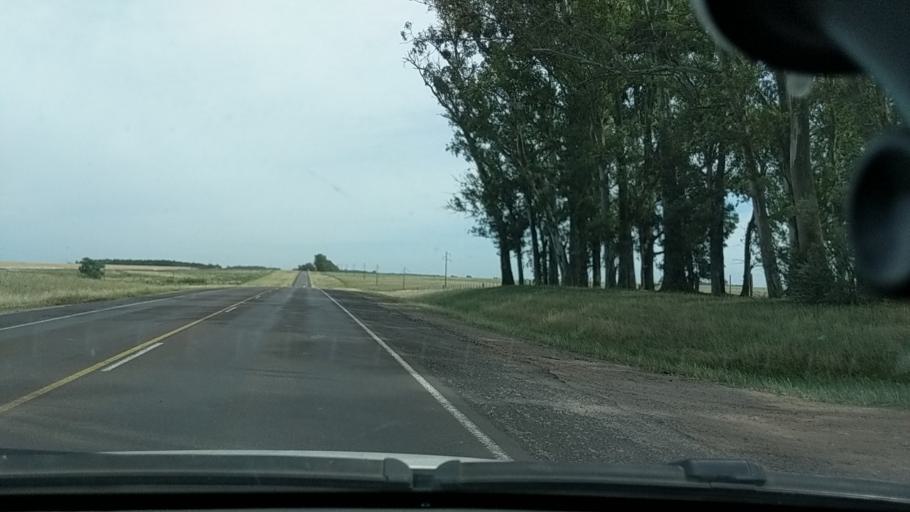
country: UY
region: Durazno
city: Durazno
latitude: -33.4831
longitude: -56.4415
